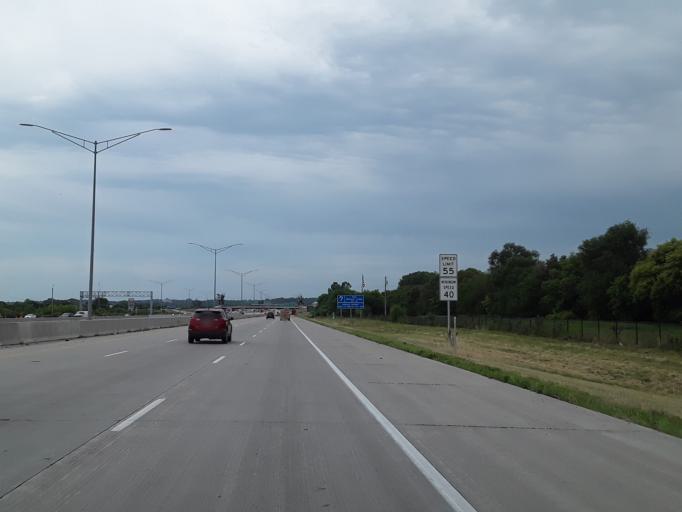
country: US
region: Iowa
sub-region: Pottawattamie County
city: Council Bluffs
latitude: 41.2327
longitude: -95.8668
